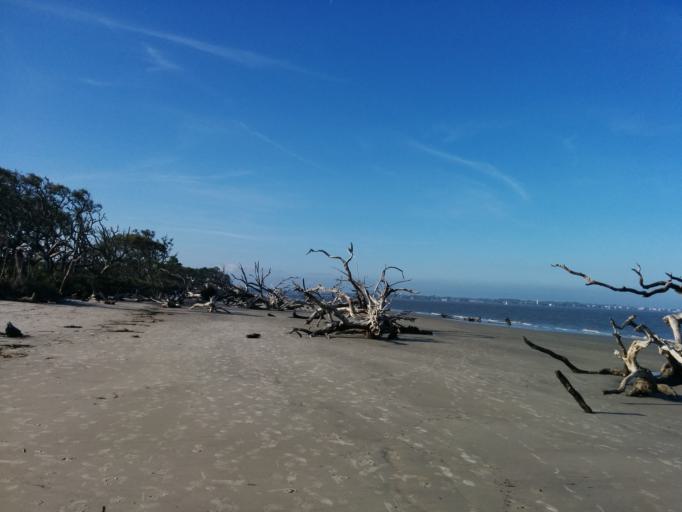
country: US
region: Georgia
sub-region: Glynn County
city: Saint Simons Island
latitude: 31.1052
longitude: -81.4045
